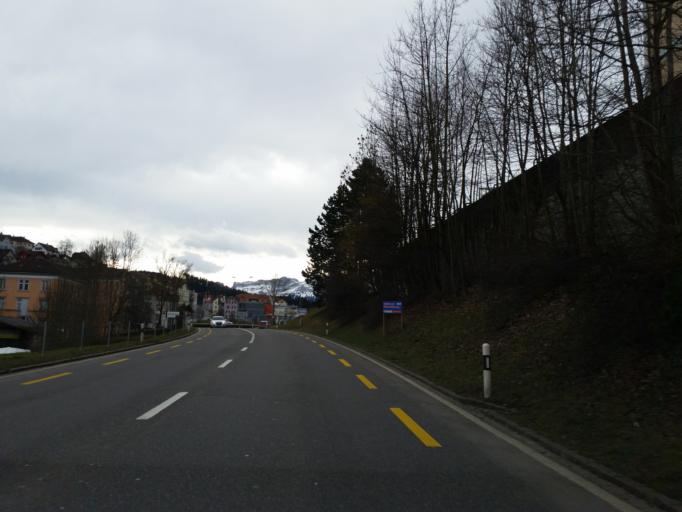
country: CH
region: Appenzell Ausserrhoden
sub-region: Bezirk Hinterland
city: Herisau
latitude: 47.3864
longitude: 9.2721
